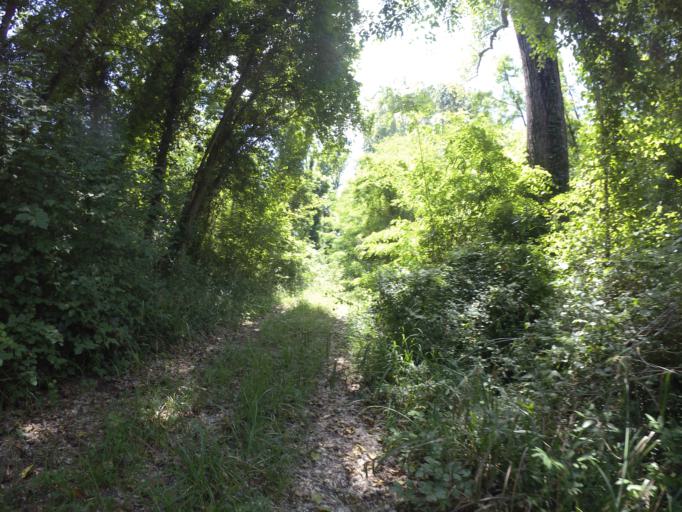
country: IT
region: Friuli Venezia Giulia
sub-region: Provincia di Udine
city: Bertiolo
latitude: 45.9294
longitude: 13.0744
